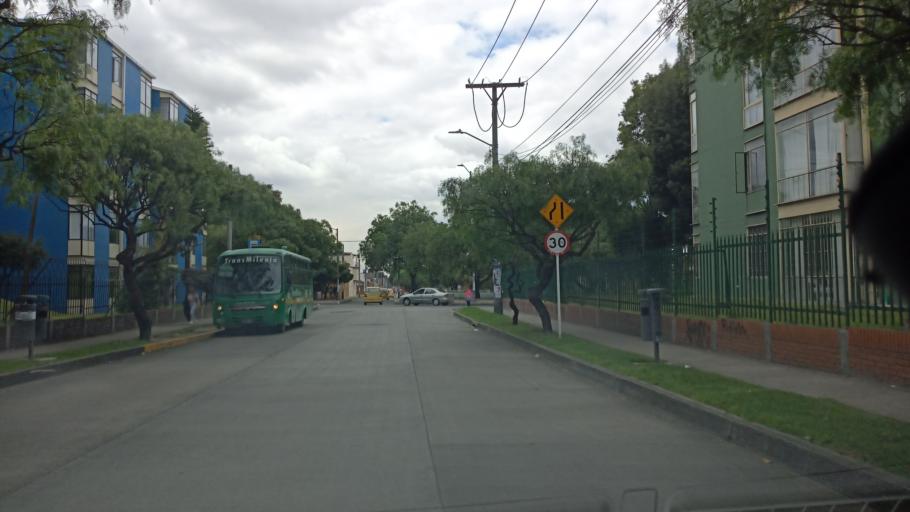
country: CO
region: Bogota D.C.
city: Bogota
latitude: 4.5738
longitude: -74.1069
